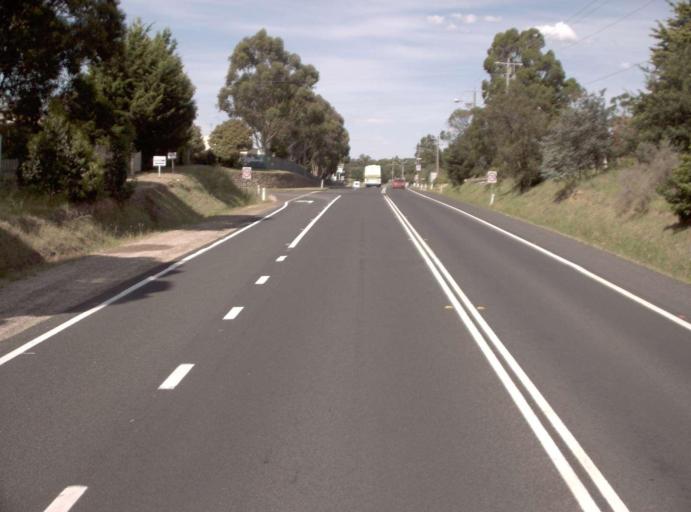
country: AU
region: Victoria
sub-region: East Gippsland
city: Bairnsdale
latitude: -37.8175
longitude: 147.7359
